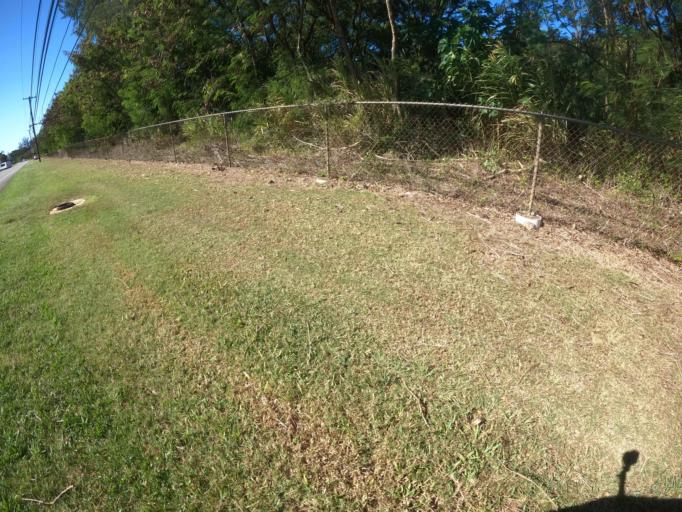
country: US
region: Hawaii
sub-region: Honolulu County
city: Kahuku
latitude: 21.6963
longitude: -158.0038
